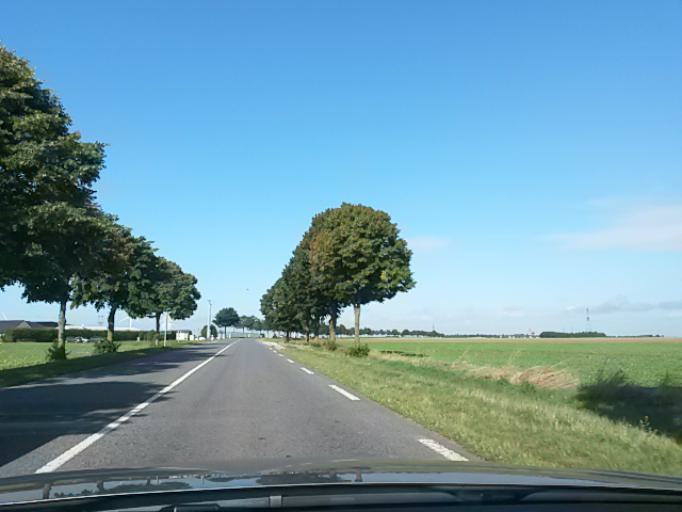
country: FR
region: Centre
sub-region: Departement d'Eure-et-Loir
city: Toury
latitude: 48.1886
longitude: 1.9210
